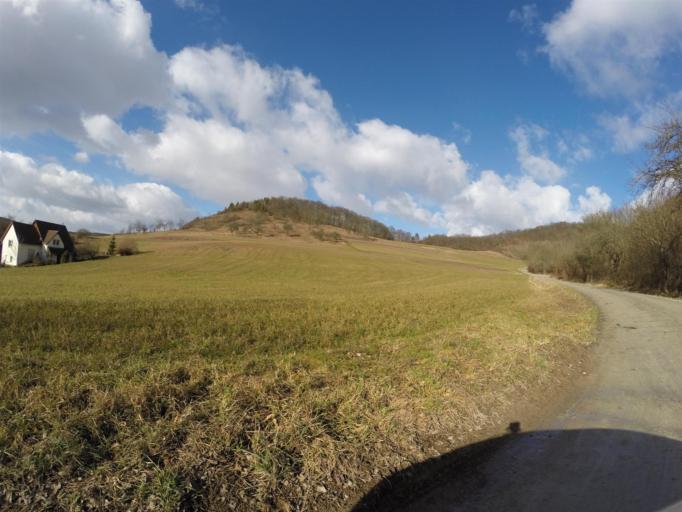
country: DE
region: Thuringia
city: Golmsdorf
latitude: 50.9746
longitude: 11.6771
